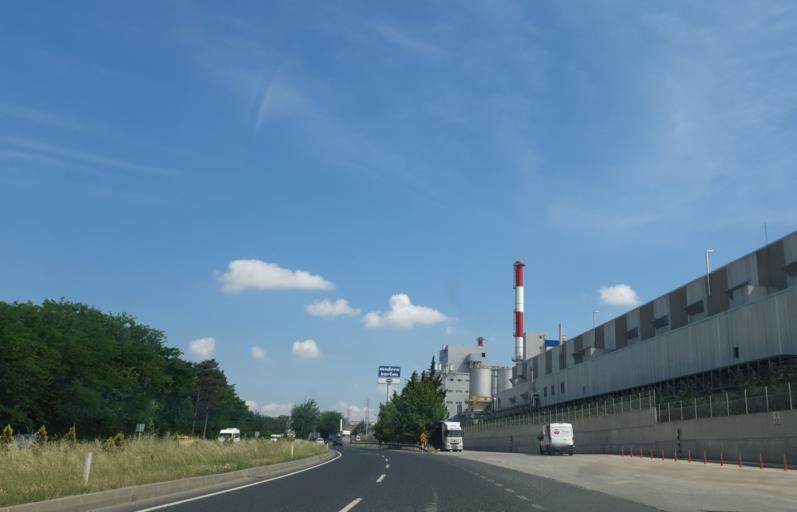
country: TR
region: Tekirdag
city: Marmaracik
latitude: 41.2414
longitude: 27.6952
